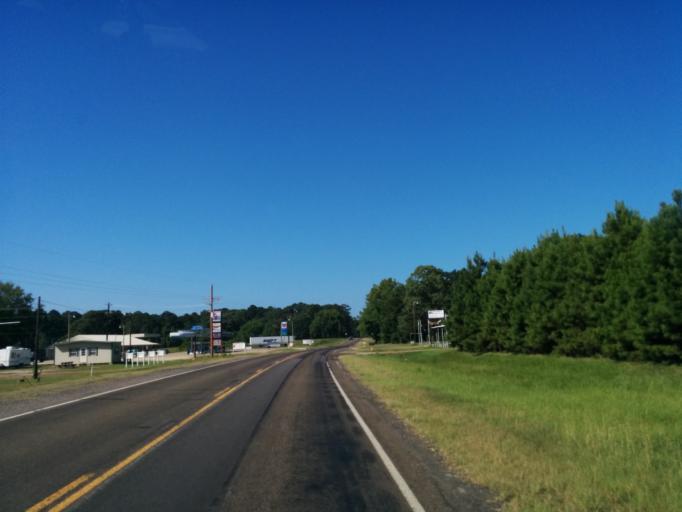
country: US
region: Texas
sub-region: Sabine County
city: Milam
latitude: 31.4508
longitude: -93.7644
